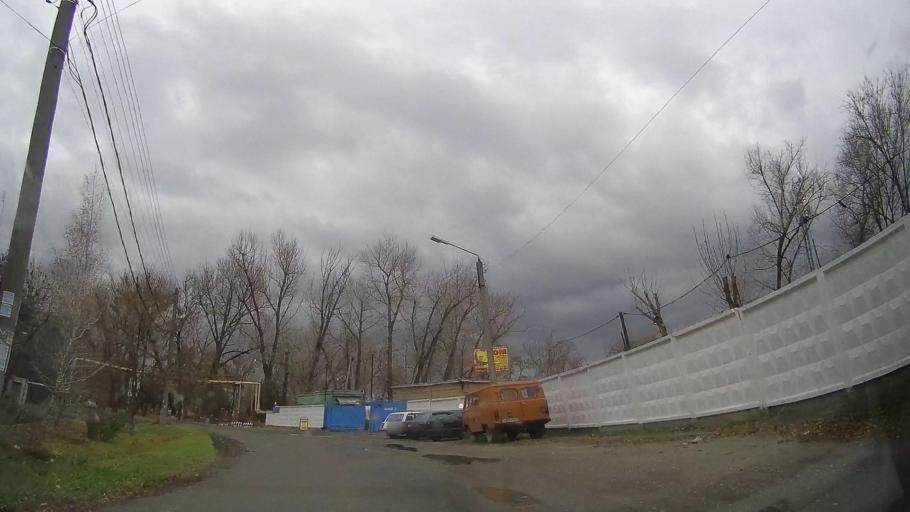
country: RU
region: Rostov
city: Bataysk
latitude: 47.1111
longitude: 39.7401
